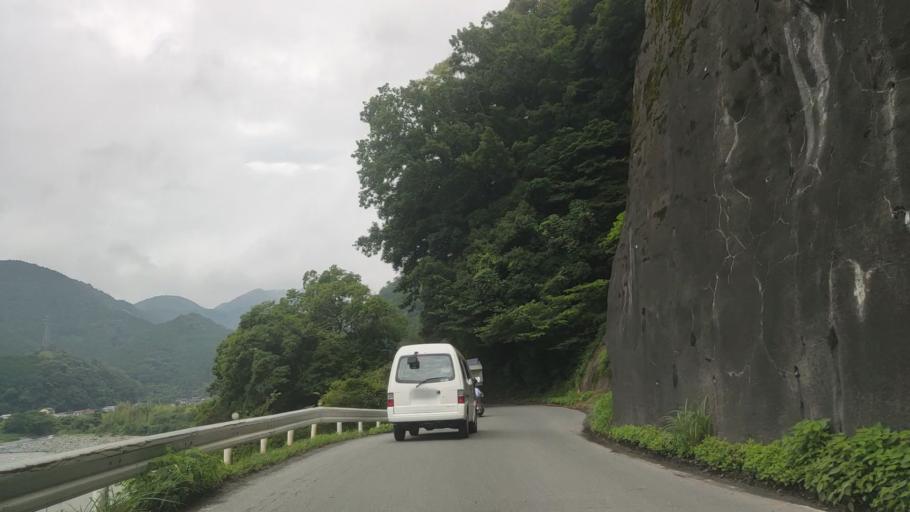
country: JP
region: Shizuoka
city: Fujinomiya
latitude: 35.2245
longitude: 138.5406
